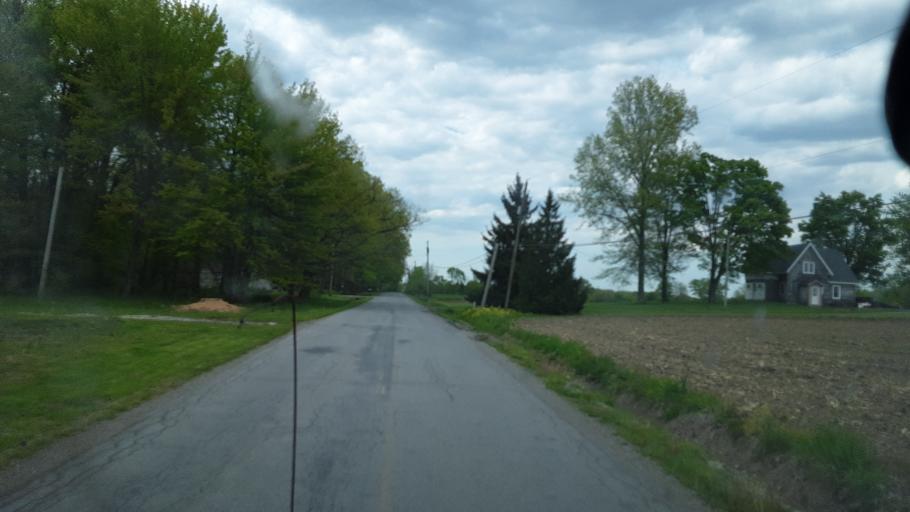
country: US
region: Ohio
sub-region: Portage County
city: Windham
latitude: 41.3011
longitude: -80.9835
